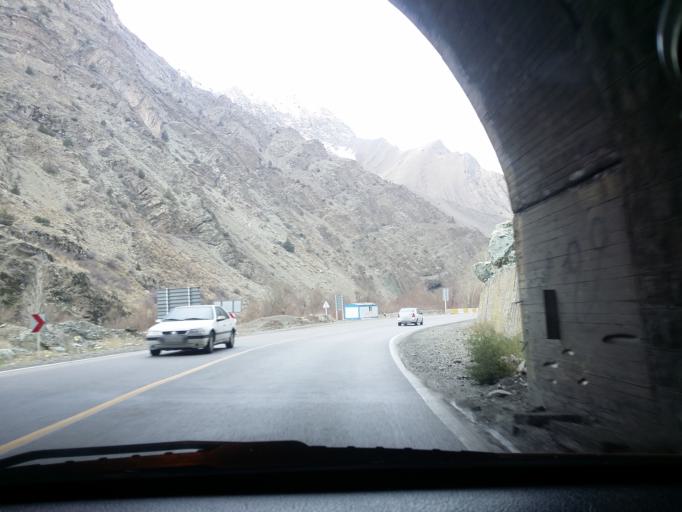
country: IR
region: Tehran
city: Tajrish
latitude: 36.0138
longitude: 51.2912
